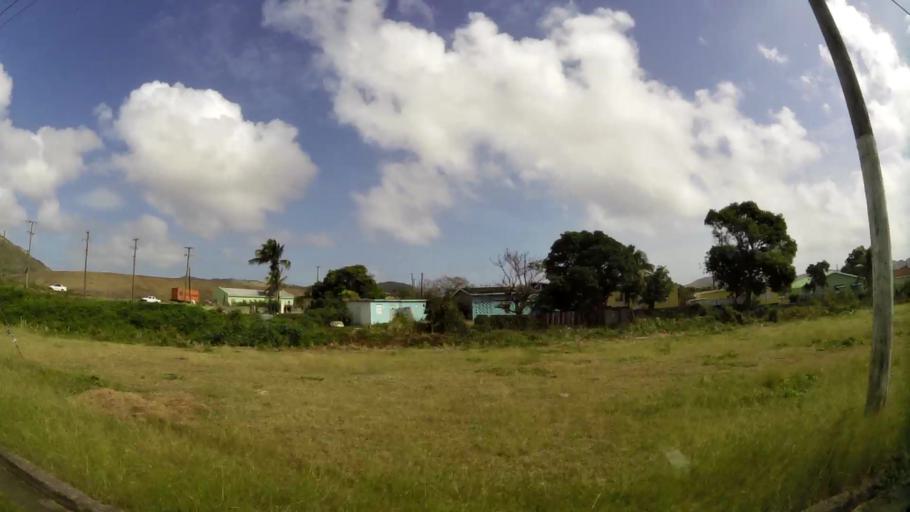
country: KN
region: Saint George Basseterre
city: Basseterre
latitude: 17.3034
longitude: -62.7278
